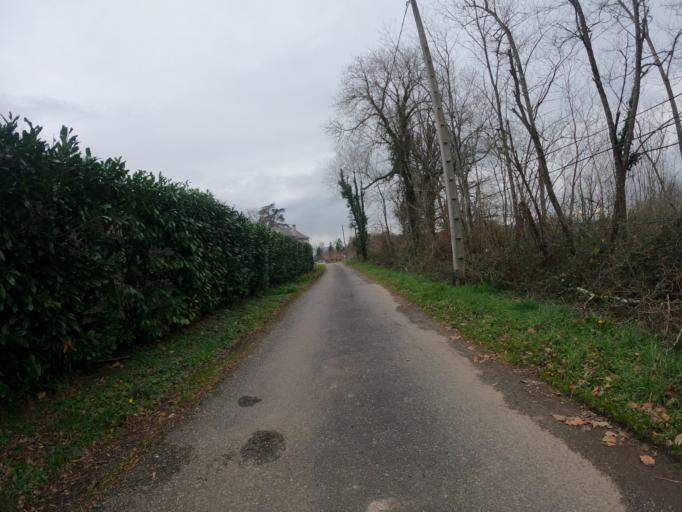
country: FR
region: Aquitaine
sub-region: Departement des Pyrenees-Atlantiques
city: Mazeres-Lezons
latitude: 43.2625
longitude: -0.3503
